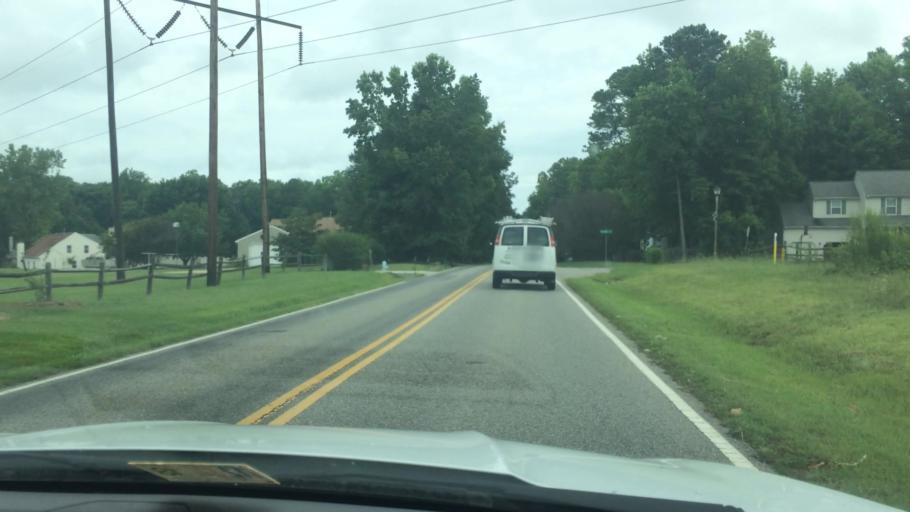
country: US
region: Virginia
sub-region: City of Williamsburg
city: Williamsburg
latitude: 37.2755
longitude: -76.6723
